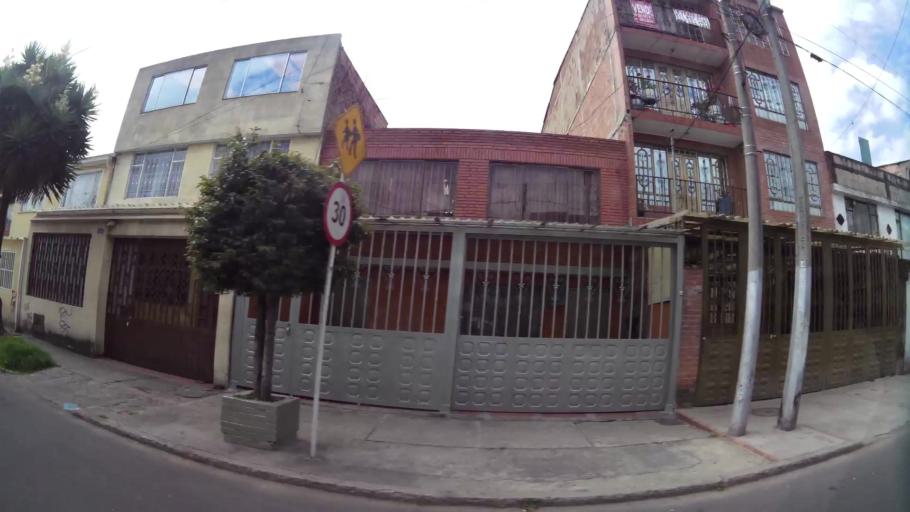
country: CO
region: Bogota D.C.
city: Bogota
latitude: 4.6151
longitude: -74.1064
